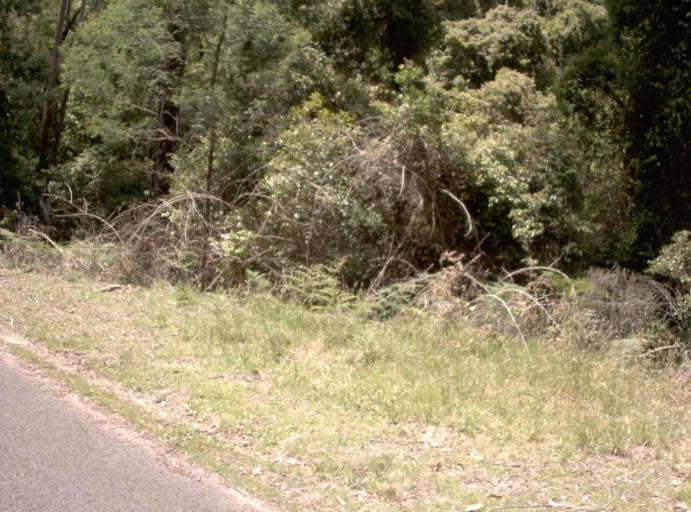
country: AU
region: New South Wales
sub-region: Bombala
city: Bombala
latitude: -37.4476
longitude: 148.9351
